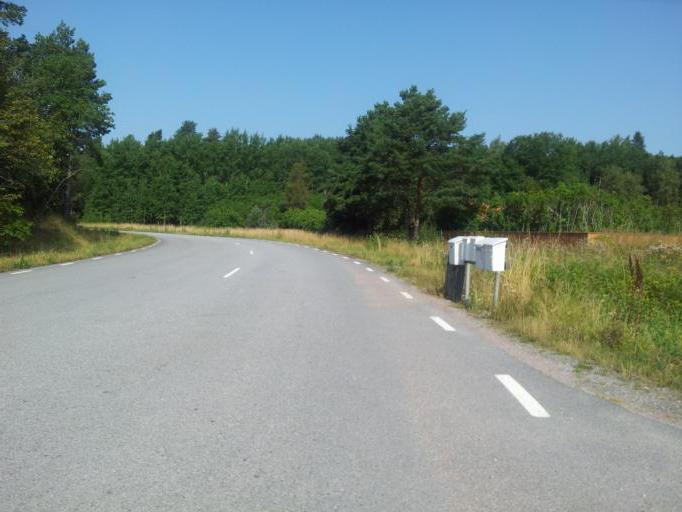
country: SE
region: Uppsala
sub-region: Uppsala Kommun
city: Gamla Uppsala
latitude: 59.8932
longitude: 17.6988
